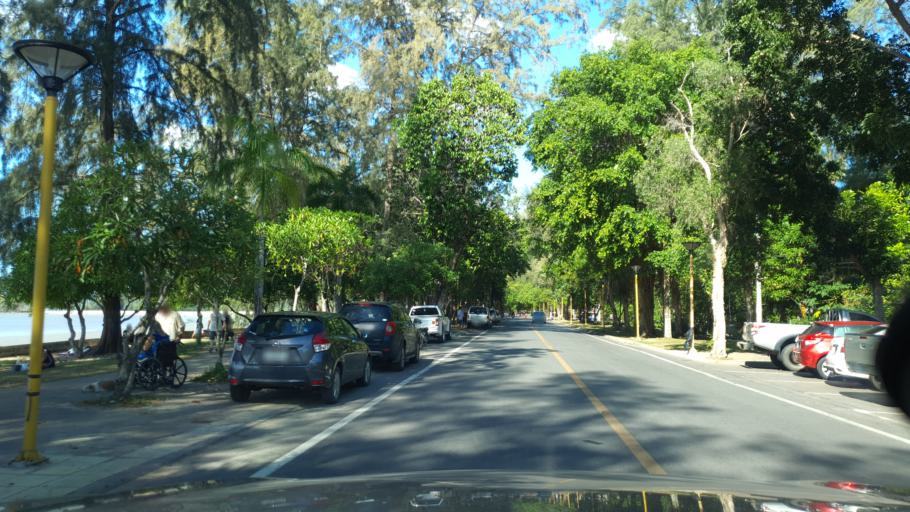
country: TH
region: Phangnga
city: Ban Ao Nang
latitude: 8.0453
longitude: 98.8048
